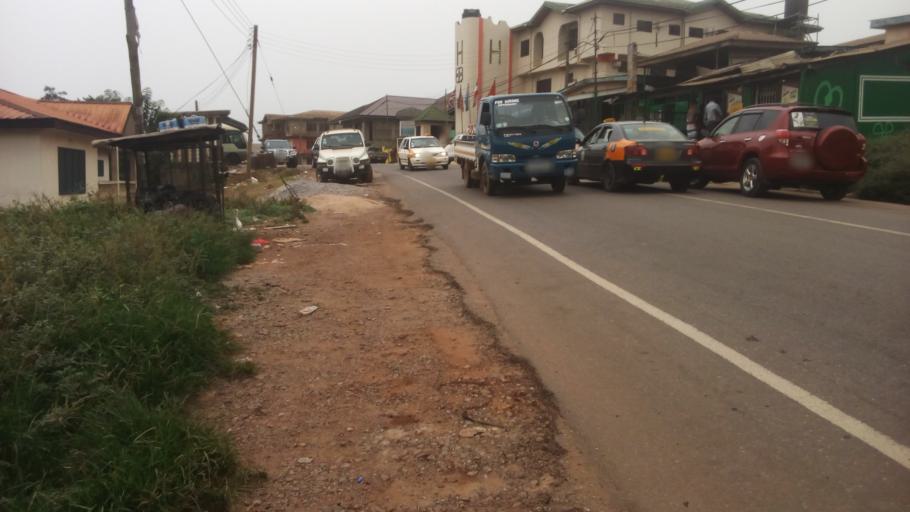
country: GH
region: Western
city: Tarkwa
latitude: 5.2869
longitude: -1.9993
